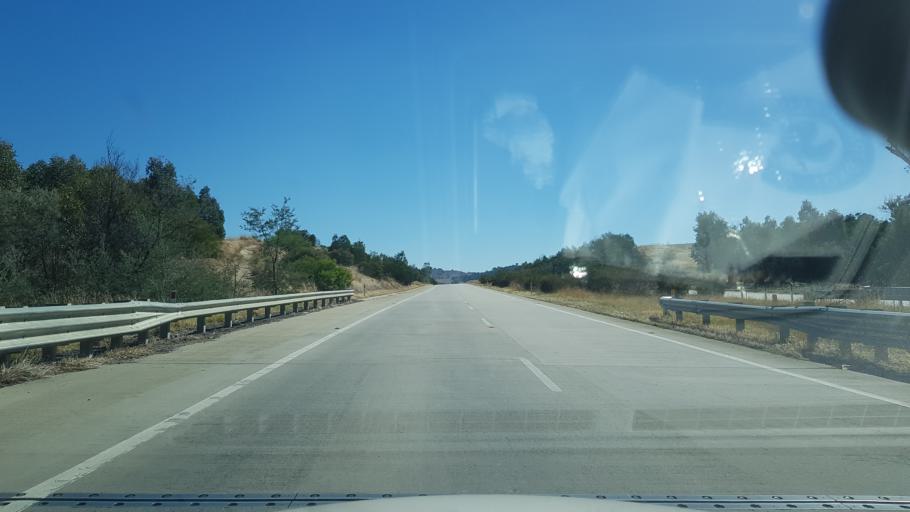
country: AU
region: New South Wales
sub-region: Albury Municipality
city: Lavington
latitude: -35.9162
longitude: 147.1403
